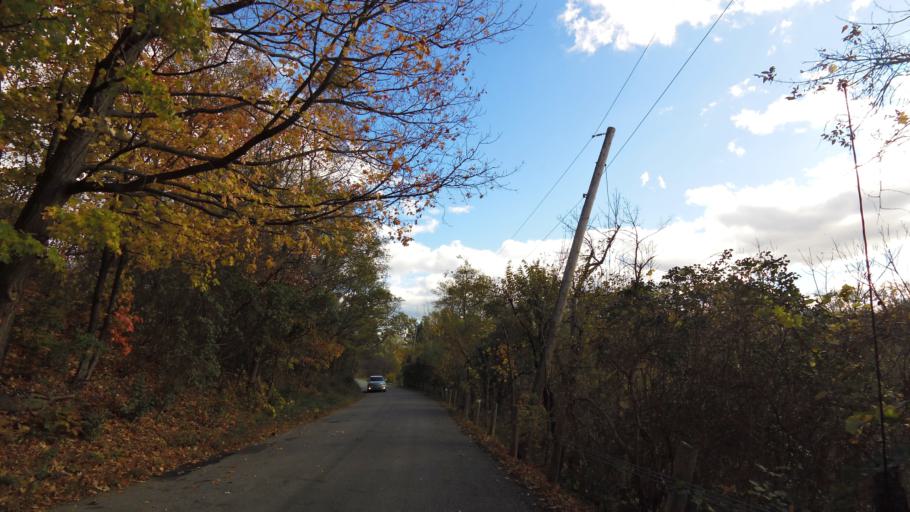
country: CA
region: Ontario
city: Burlington
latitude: 43.4403
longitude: -79.8402
